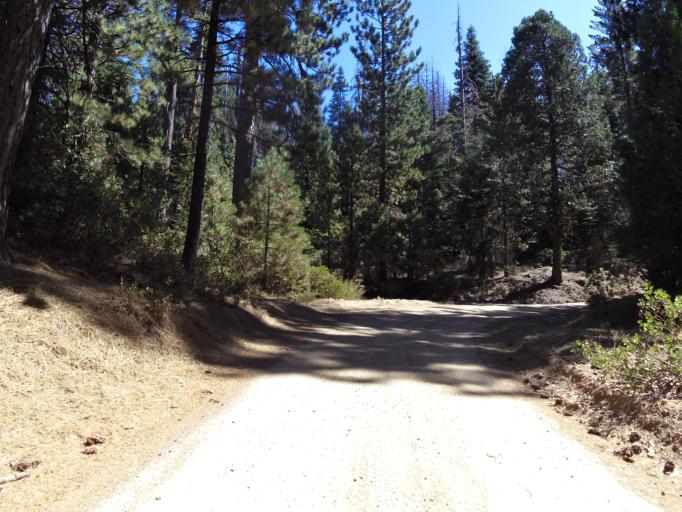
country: US
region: California
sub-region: Madera County
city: Oakhurst
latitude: 37.4399
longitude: -119.5358
